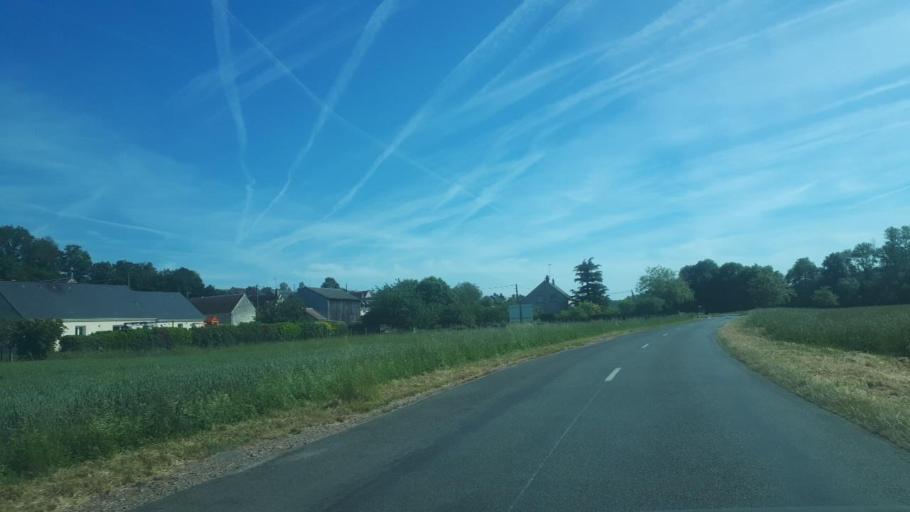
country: FR
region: Centre
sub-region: Departement du Loir-et-Cher
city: Villiers-sur-Loir
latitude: 47.8284
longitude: 0.9756
